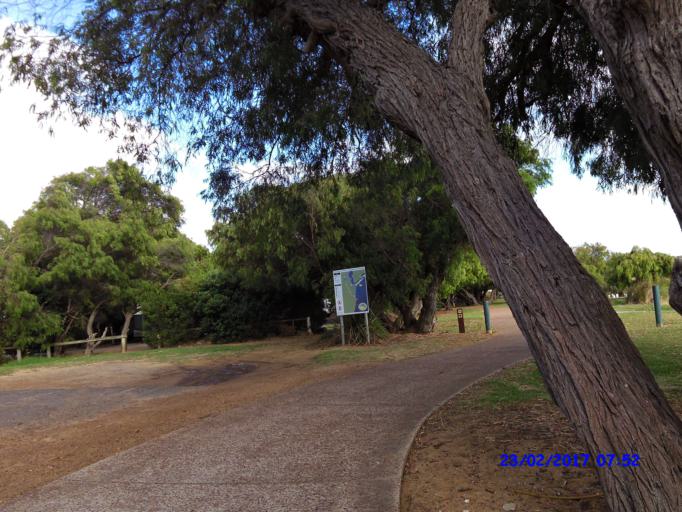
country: AU
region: Western Australia
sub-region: Augusta-Margaret River Shire
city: Augusta
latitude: -34.3245
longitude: 115.1660
